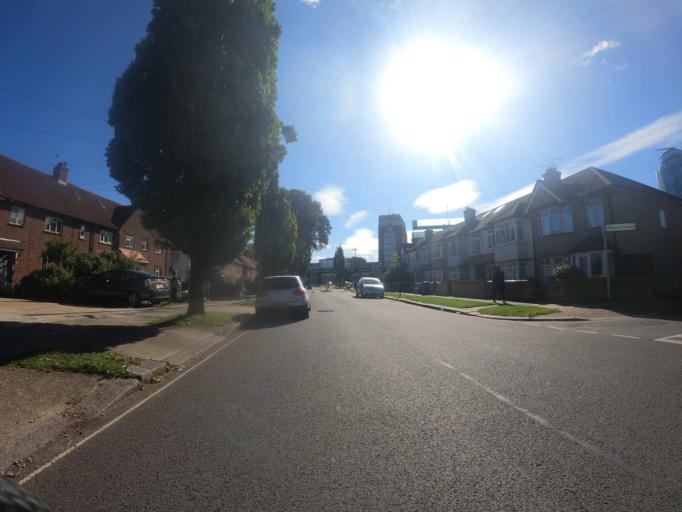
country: GB
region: England
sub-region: Greater London
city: Brentford
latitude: 51.4927
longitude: -0.3001
